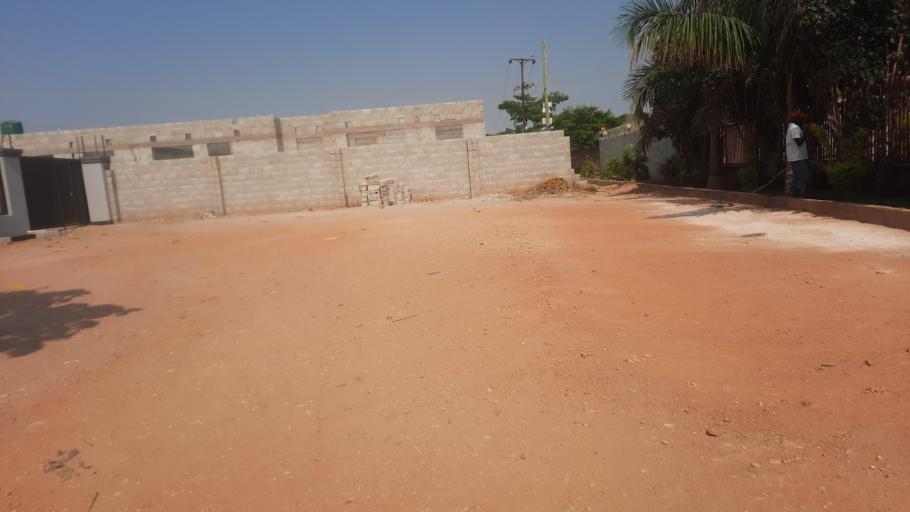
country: ZM
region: Lusaka
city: Lusaka
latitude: -15.3942
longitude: 28.3877
